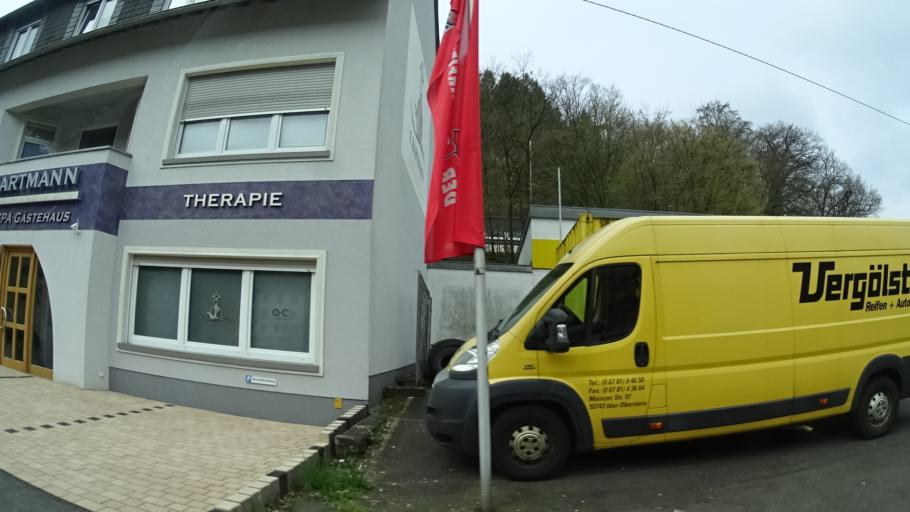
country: DE
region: Rheinland-Pfalz
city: Idar-Oberstein
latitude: 49.7153
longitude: 7.3074
